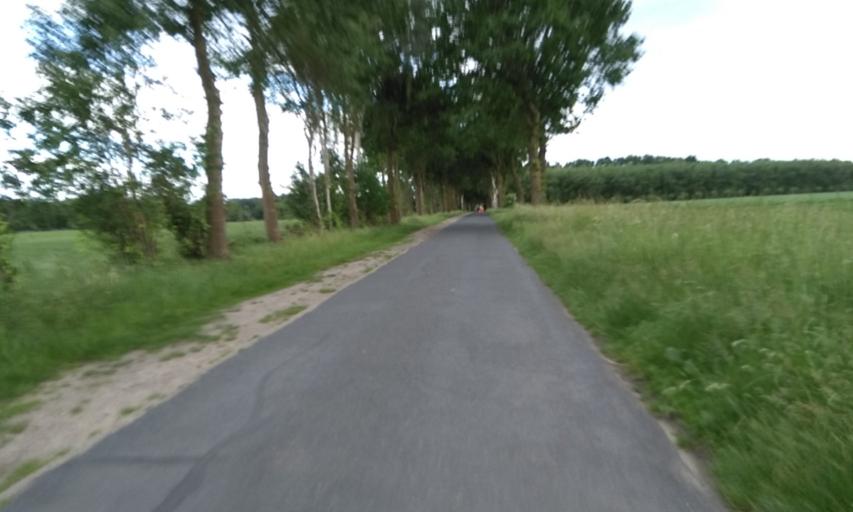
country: DE
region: Lower Saxony
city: Regesbostel
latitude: 53.3859
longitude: 9.6436
